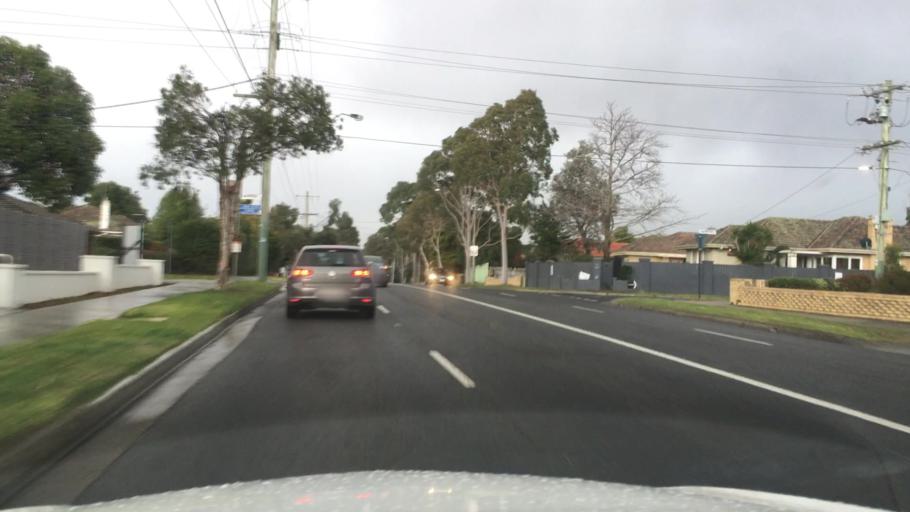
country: AU
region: Victoria
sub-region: Monash
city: Ashwood
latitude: -37.8765
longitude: 145.1101
